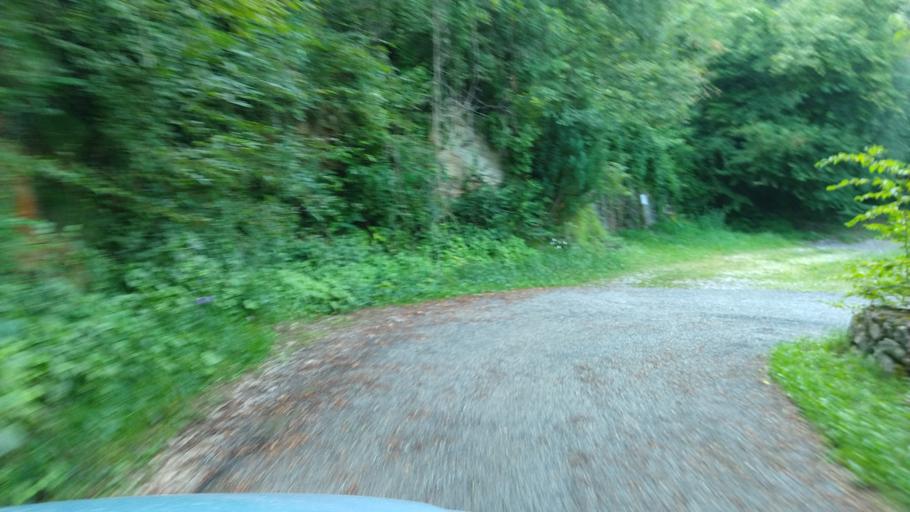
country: IT
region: Veneto
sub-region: Provincia di Vicenza
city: San Nazario
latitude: 45.8284
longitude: 11.6889
